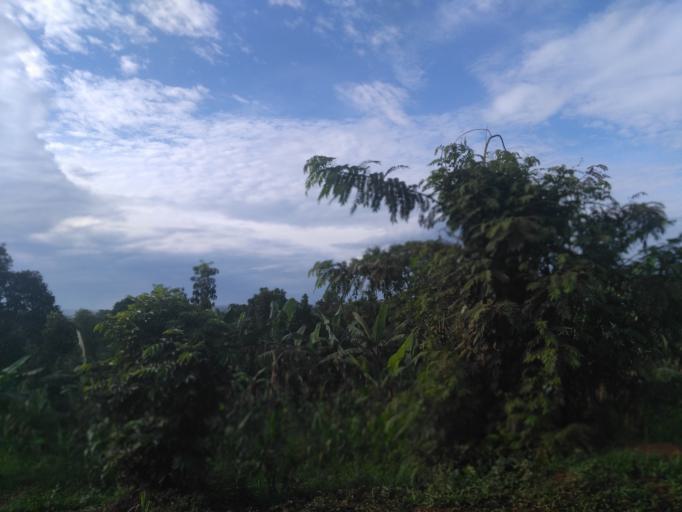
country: UG
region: Eastern Region
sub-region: Jinja District
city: Jinja
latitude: 0.4653
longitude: 33.1772
